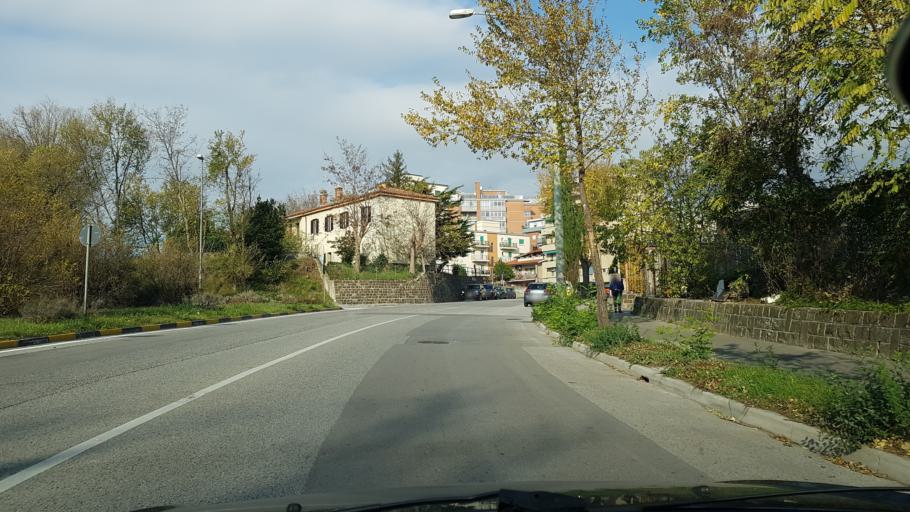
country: IT
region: Friuli Venezia Giulia
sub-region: Provincia di Trieste
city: Trieste
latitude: 45.6200
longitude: 13.8003
